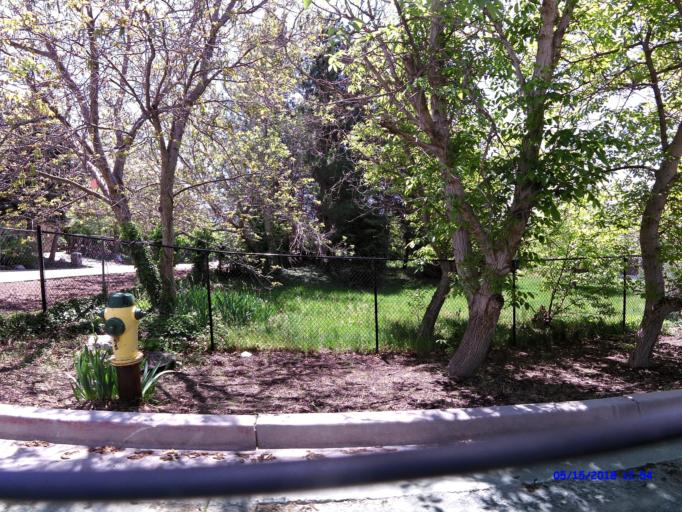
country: US
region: Utah
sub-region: Weber County
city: Uintah
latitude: 41.1598
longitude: -111.9188
